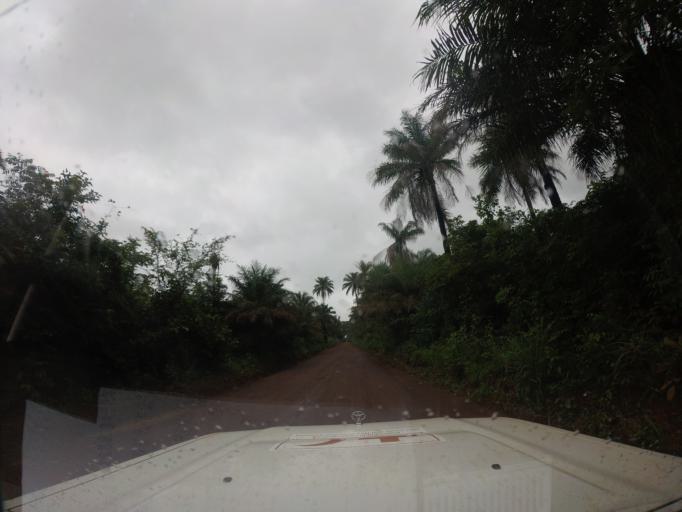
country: SL
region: Northern Province
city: Kambia
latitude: 9.1340
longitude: -12.8825
